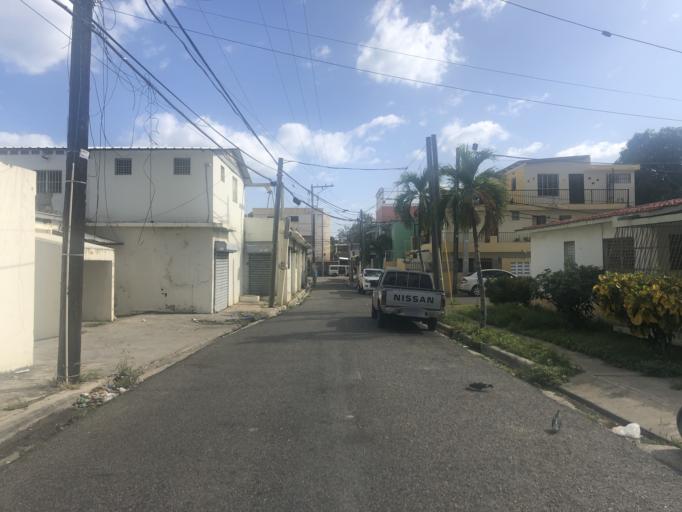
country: DO
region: Nacional
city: La Julia
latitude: 18.4551
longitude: -69.9272
